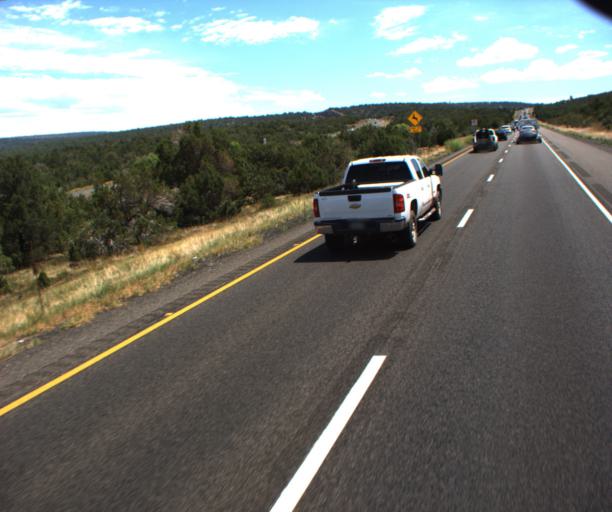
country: US
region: Arizona
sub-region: Yavapai County
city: Village of Oak Creek (Big Park)
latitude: 34.7812
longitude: -111.6155
